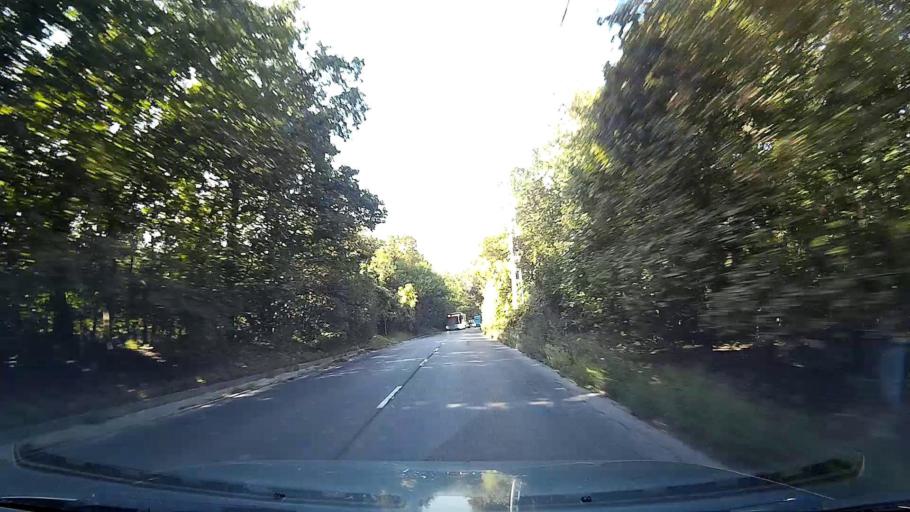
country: HU
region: Pest
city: Budaors
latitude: 47.4324
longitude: 18.9798
